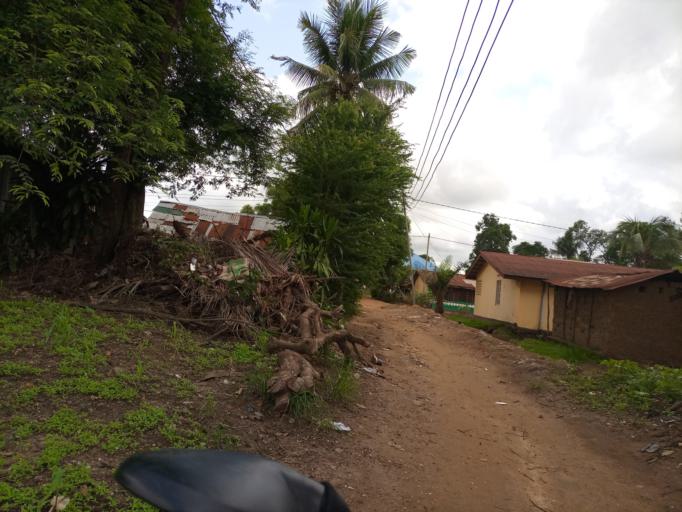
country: SL
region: Southern Province
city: Bo
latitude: 7.9619
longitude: -11.7594
